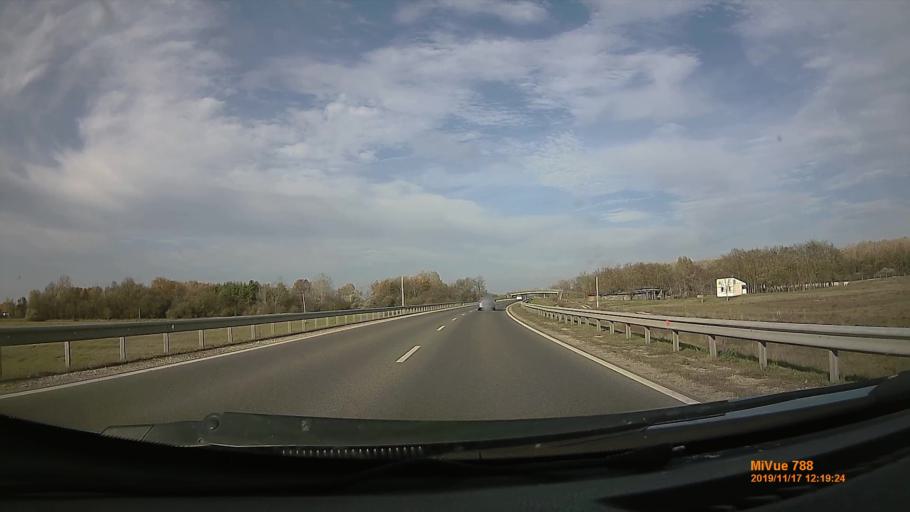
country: HU
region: Bacs-Kiskun
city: Kecskemet
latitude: 46.9293
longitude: 19.7151
